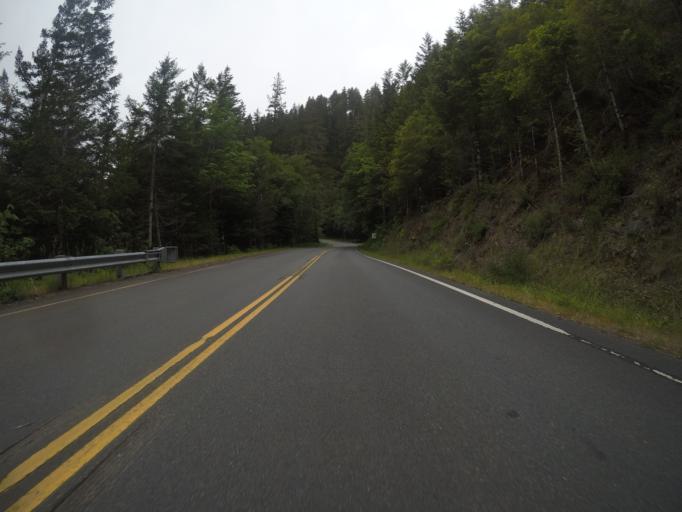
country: US
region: California
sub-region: Del Norte County
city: Bertsch-Oceanview
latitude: 41.7740
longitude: -124.0152
